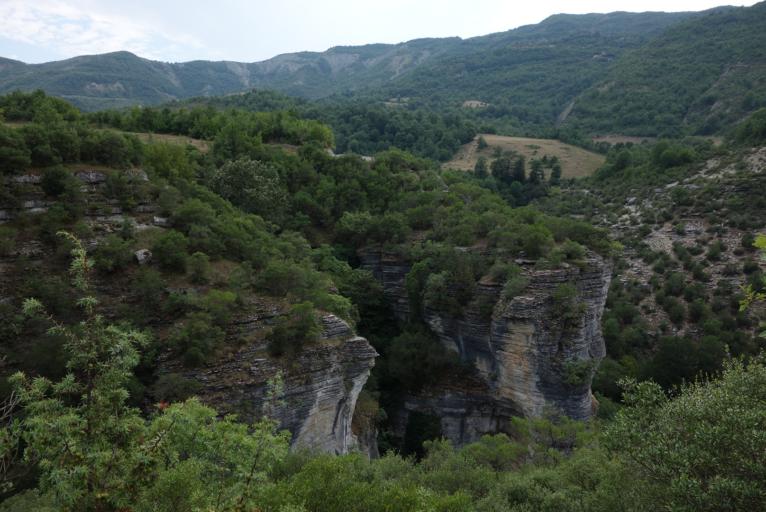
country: AL
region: Berat
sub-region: Rrethi i Skraparit
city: Cepan
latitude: 40.4350
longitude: 20.2842
